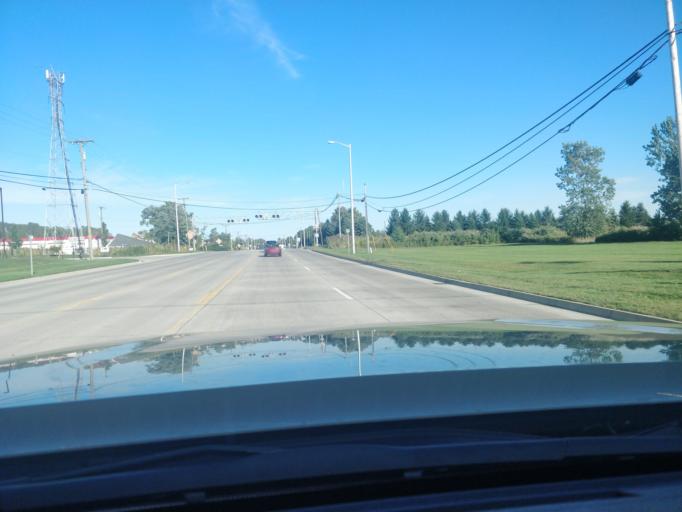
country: US
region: Michigan
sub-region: Wayne County
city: Woodhaven
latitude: 42.1694
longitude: -83.2337
